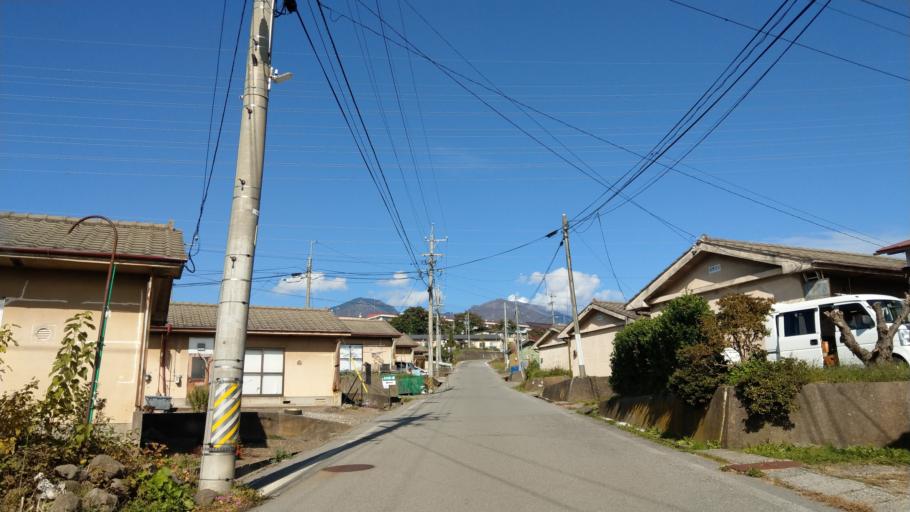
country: JP
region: Nagano
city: Komoro
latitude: 36.3272
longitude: 138.4417
